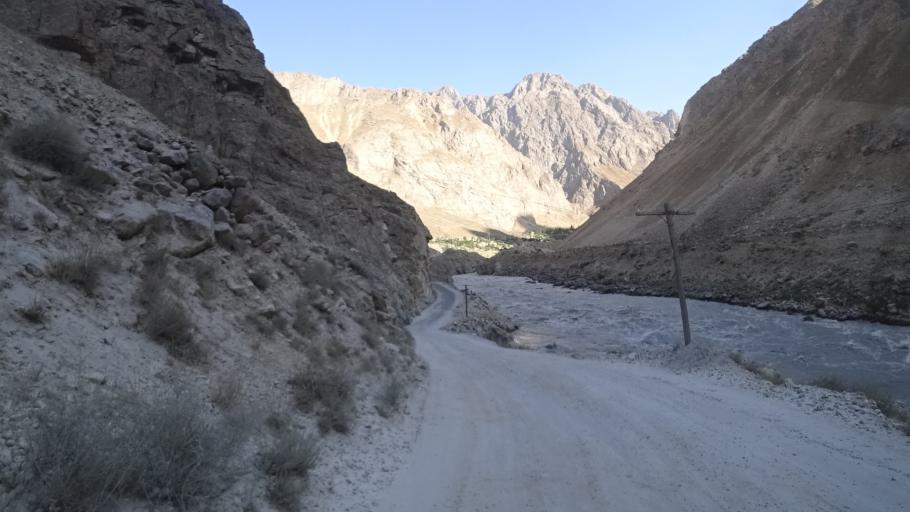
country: TJ
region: Gorno-Badakhshan
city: Rushon
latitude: 37.9806
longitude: 71.2705
